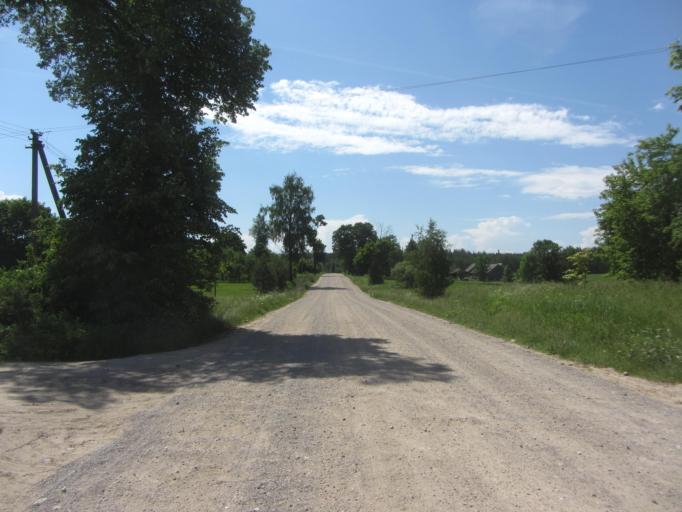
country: LT
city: Jieznas
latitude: 54.6512
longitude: 24.3083
